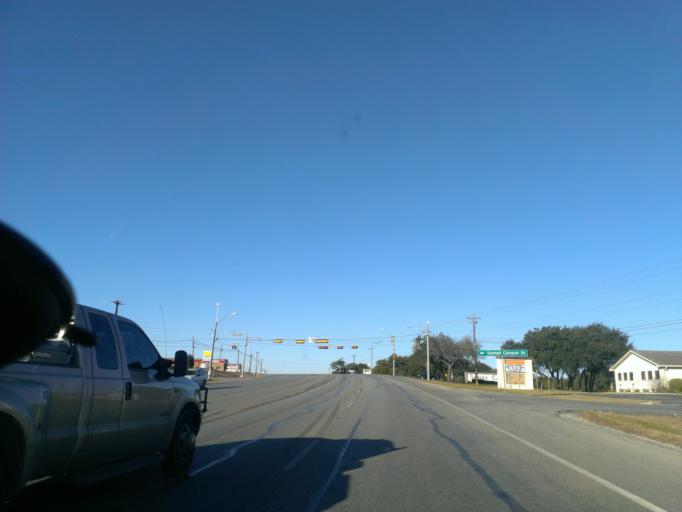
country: US
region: Texas
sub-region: Hays County
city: Dripping Springs
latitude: 30.1974
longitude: -98.0186
